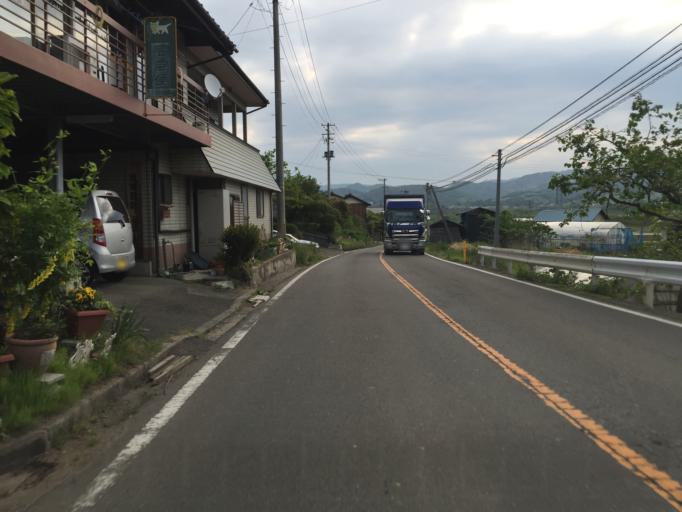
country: JP
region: Fukushima
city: Yanagawamachi-saiwaicho
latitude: 37.8735
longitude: 140.6055
